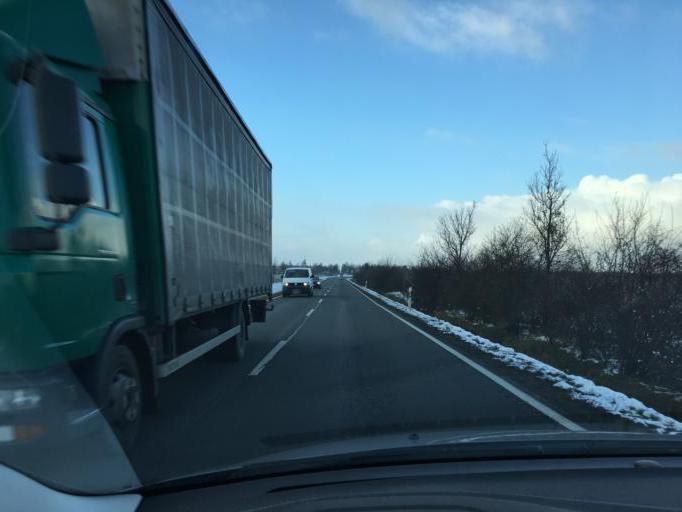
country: DE
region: Saxony
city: Brandis
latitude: 51.3464
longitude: 12.5955
